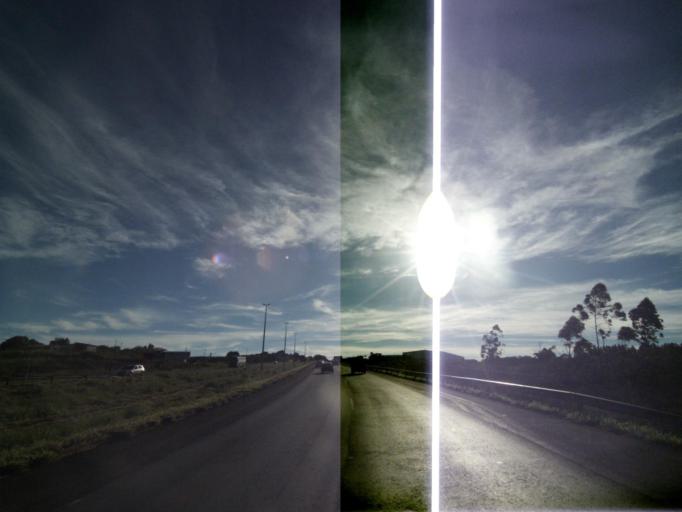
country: BR
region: Federal District
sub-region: Brasilia
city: Brasilia
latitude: -15.7897
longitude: -48.2248
